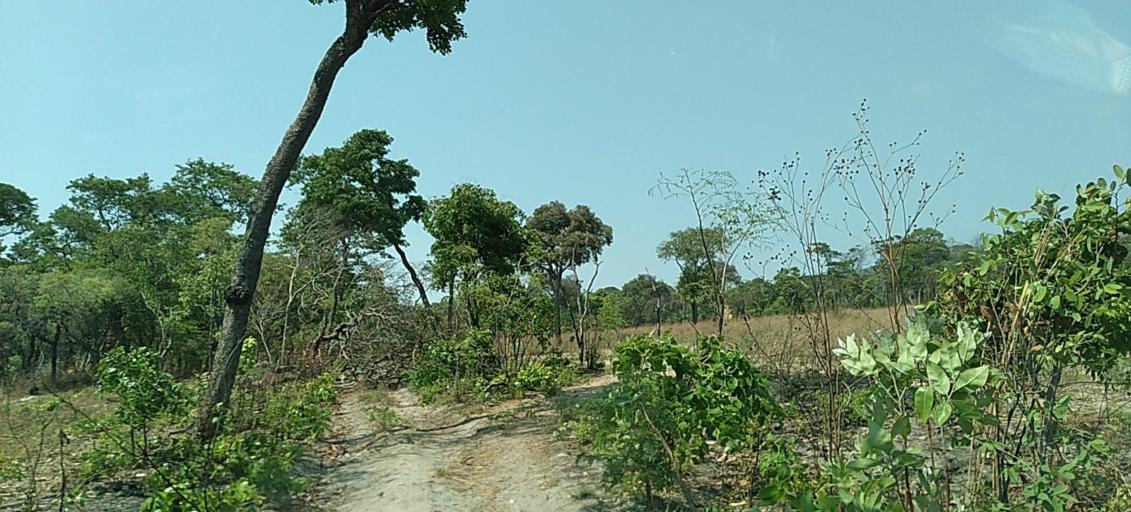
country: ZM
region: Copperbelt
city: Mpongwe
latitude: -13.7867
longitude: 28.0988
